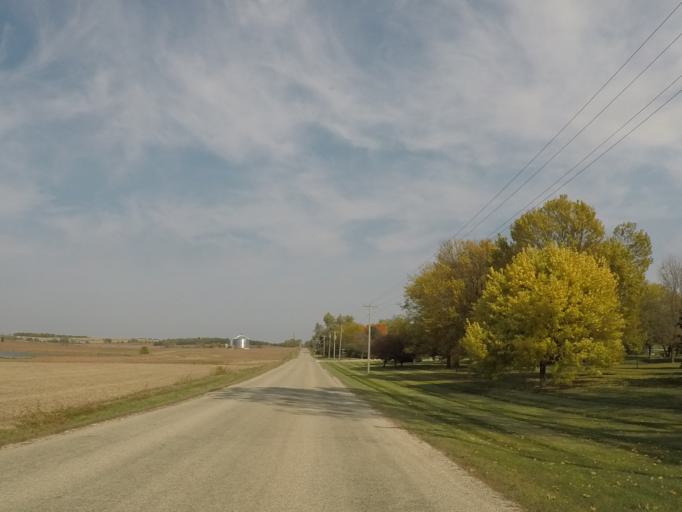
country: US
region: Wisconsin
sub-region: Dane County
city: Cross Plains
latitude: 43.0529
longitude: -89.6009
